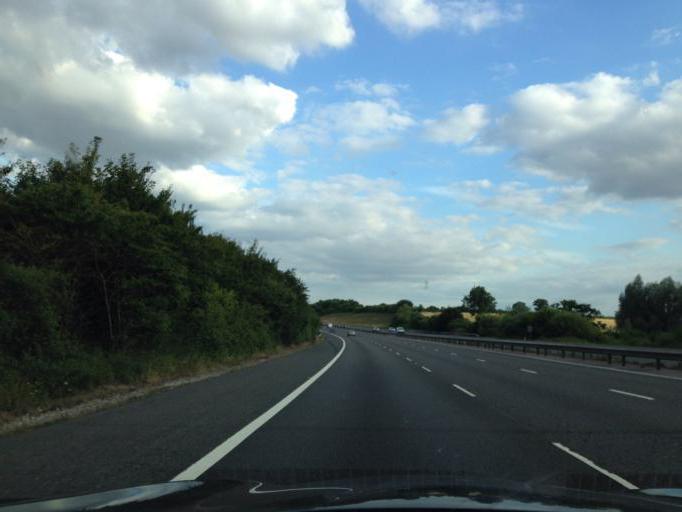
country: GB
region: England
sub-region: Oxfordshire
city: Wheatley
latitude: 51.8141
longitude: -1.1038
